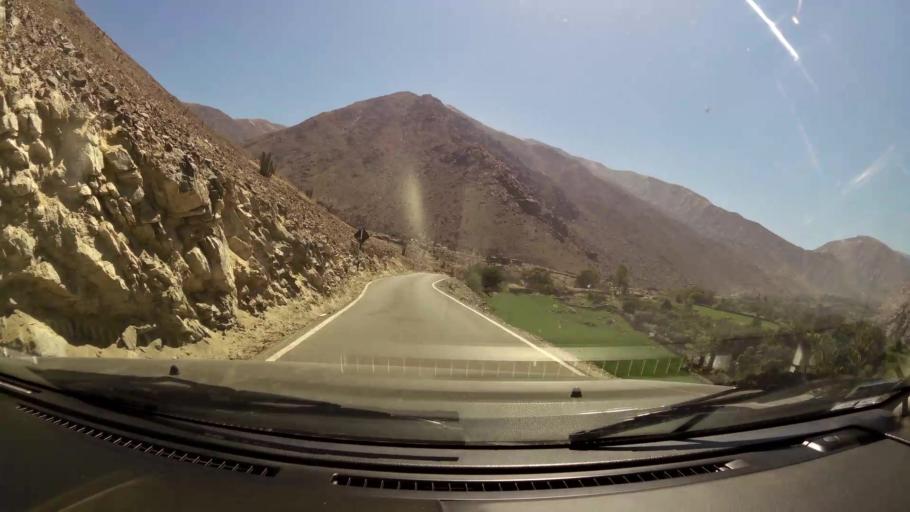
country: PE
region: Ica
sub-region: Provincia de Pisco
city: Huancano
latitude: -13.8285
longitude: -75.5402
